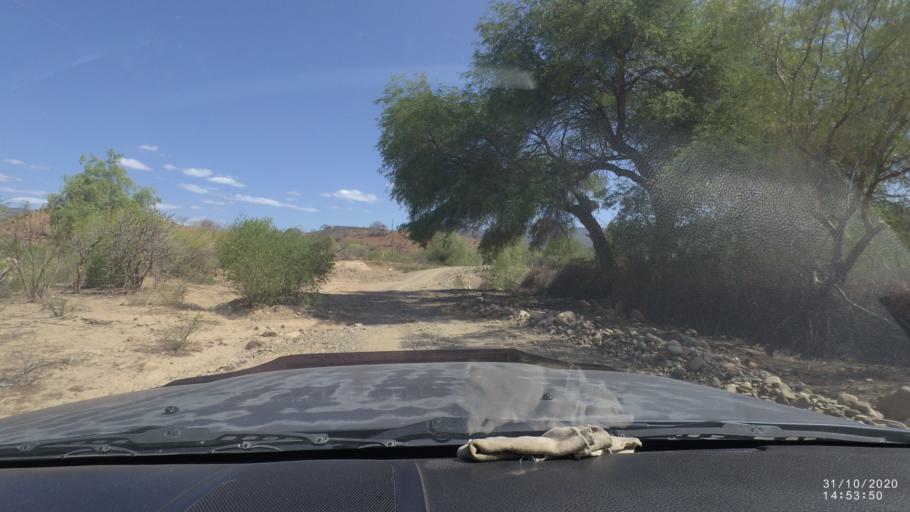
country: BO
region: Cochabamba
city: Aiquile
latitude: -18.2221
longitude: -64.8572
